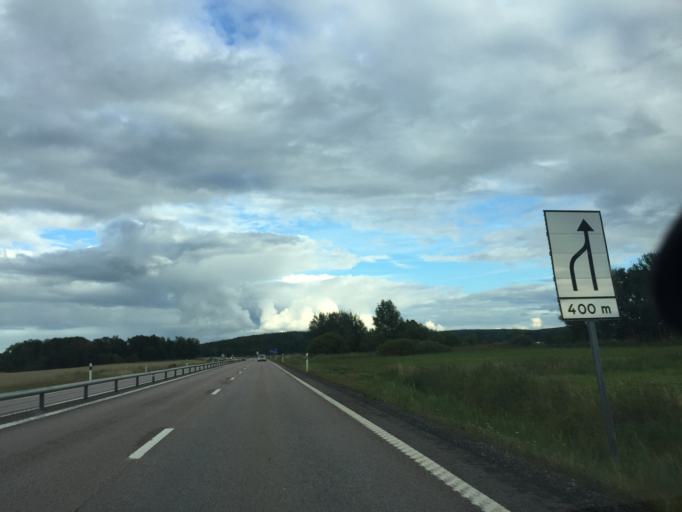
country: SE
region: Vaestmanland
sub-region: Arboga Kommun
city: Tyringe
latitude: 59.3973
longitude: 15.9061
